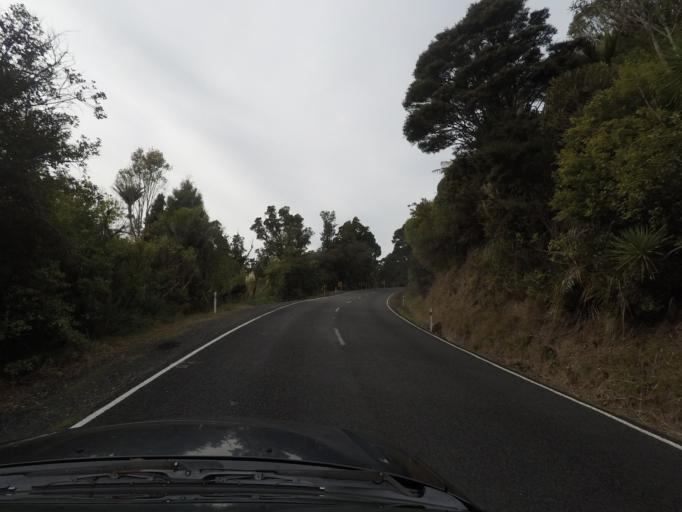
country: NZ
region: Auckland
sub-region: Auckland
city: Titirangi
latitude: -36.9421
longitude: 174.5944
